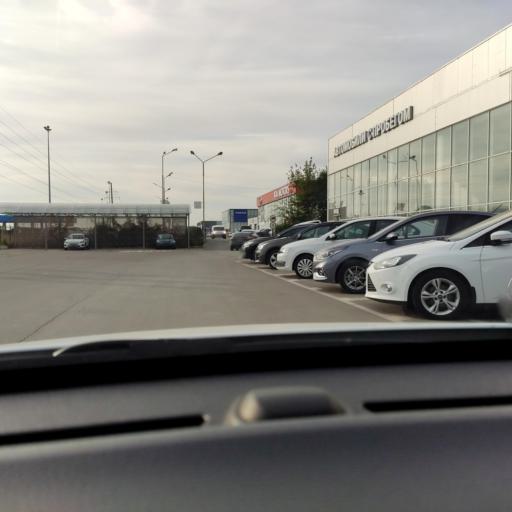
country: RU
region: Voronezj
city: Somovo
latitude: 51.6649
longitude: 39.3002
